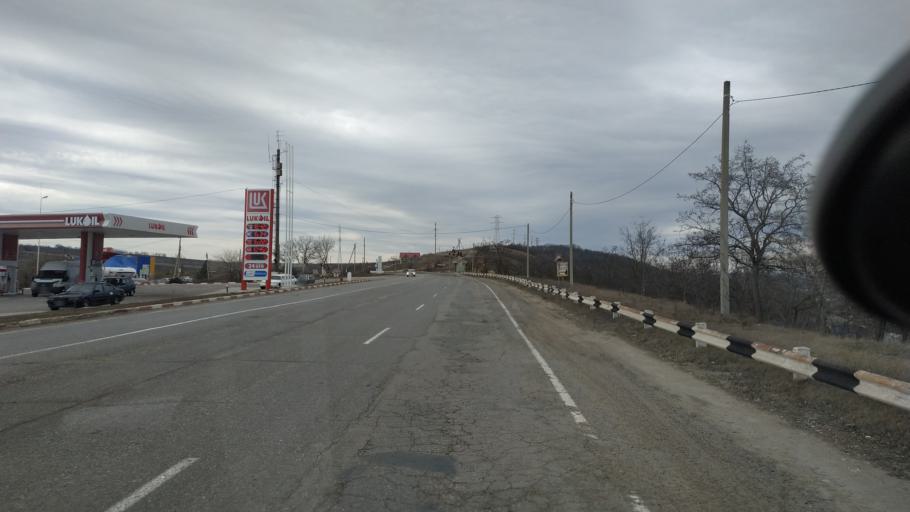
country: MD
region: Chisinau
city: Vadul lui Voda
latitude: 47.0879
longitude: 29.0719
